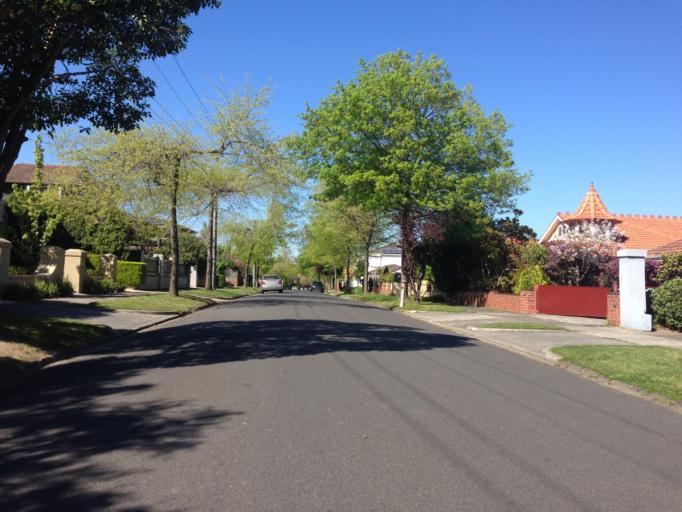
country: AU
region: Victoria
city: Balwyn
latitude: -37.8026
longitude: 145.0693
